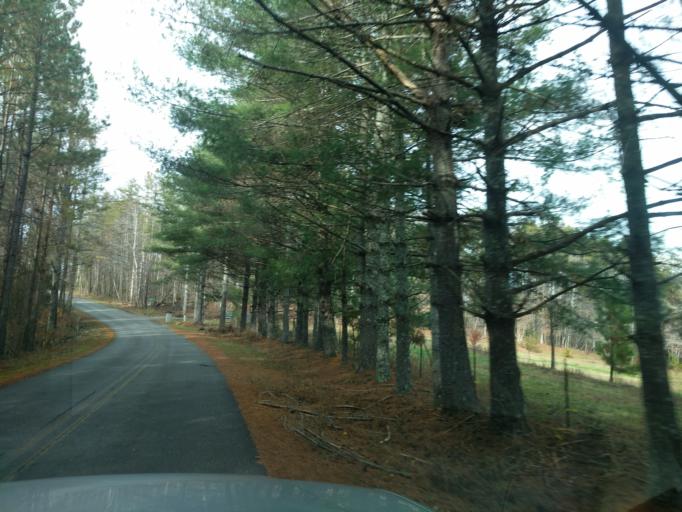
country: US
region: South Carolina
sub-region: Oconee County
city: Walhalla
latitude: 34.8578
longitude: -83.0546
